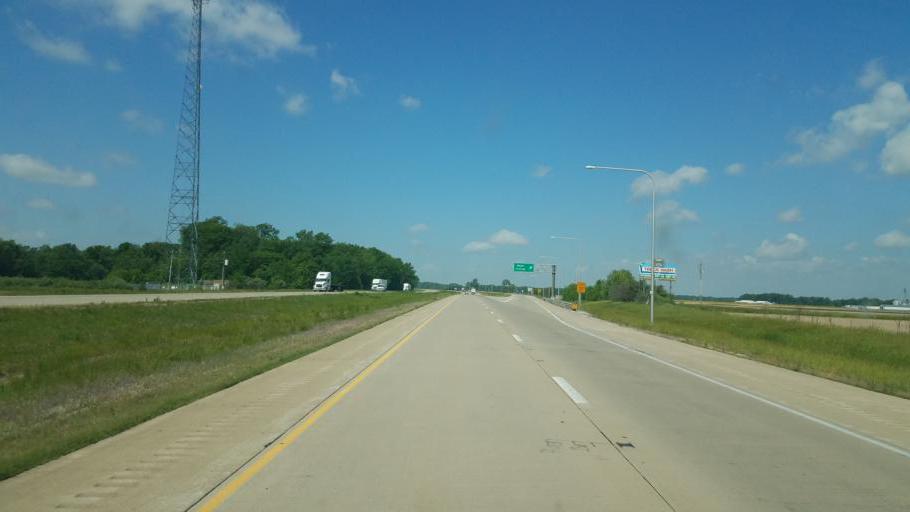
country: US
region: Illinois
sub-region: Clark County
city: Marshall
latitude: 39.4256
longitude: -87.6086
